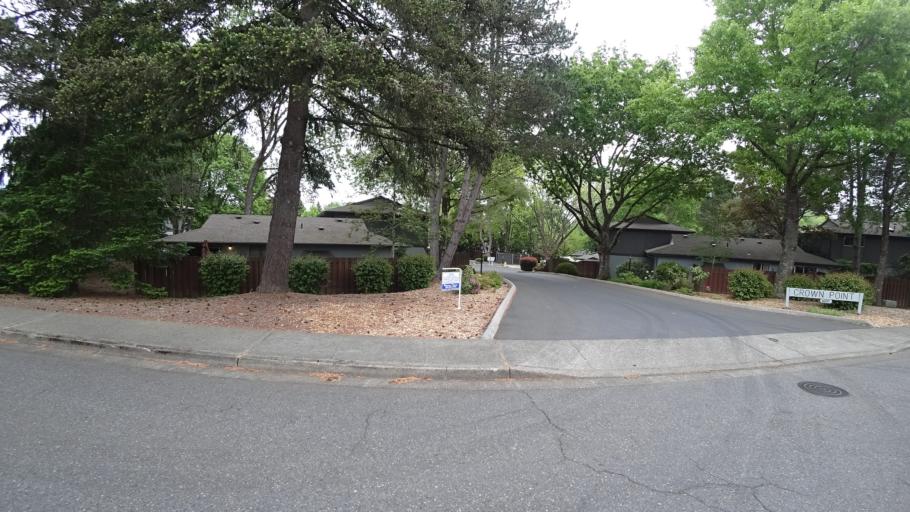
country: US
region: Oregon
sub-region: Washington County
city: Beaverton
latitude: 45.4747
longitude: -122.8108
